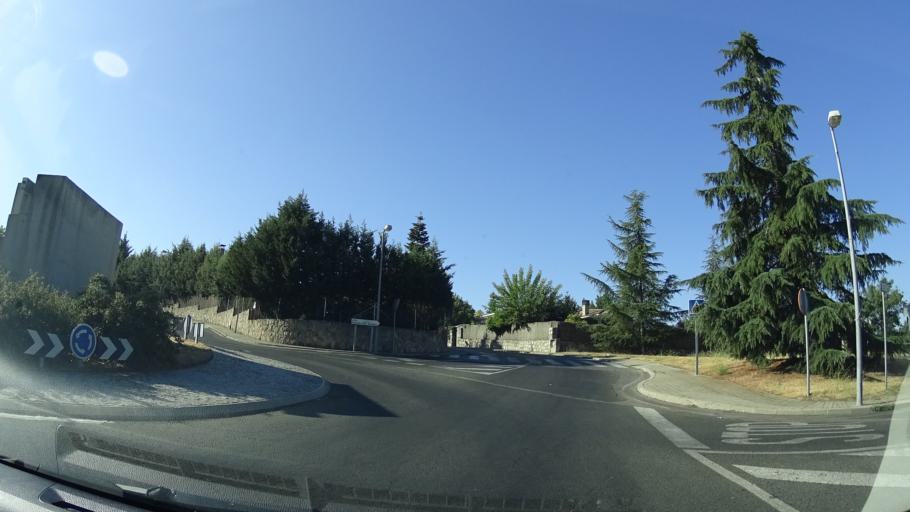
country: ES
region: Madrid
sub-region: Provincia de Madrid
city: Colmenarejo
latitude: 40.5563
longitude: -4.0234
